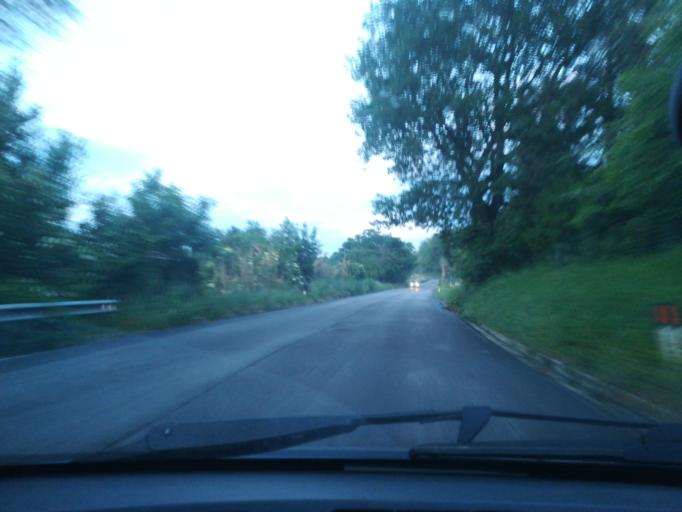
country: IT
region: The Marches
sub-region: Provincia di Macerata
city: Sforzacosta
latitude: 43.2877
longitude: 13.4050
